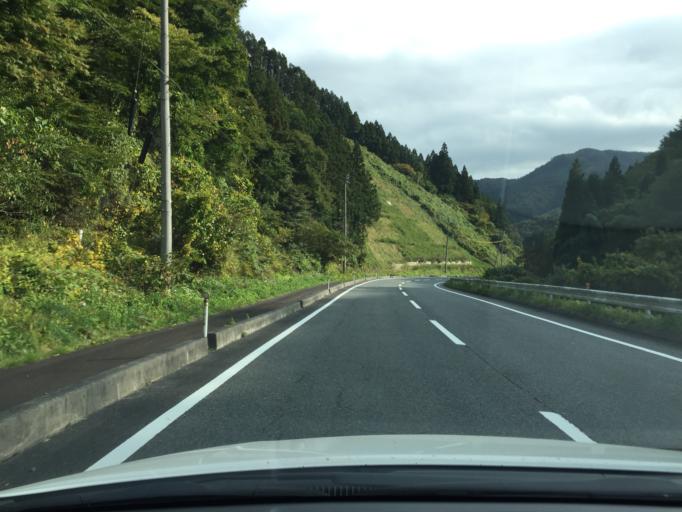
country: JP
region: Ibaraki
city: Kitaibaraki
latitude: 36.9555
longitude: 140.6246
